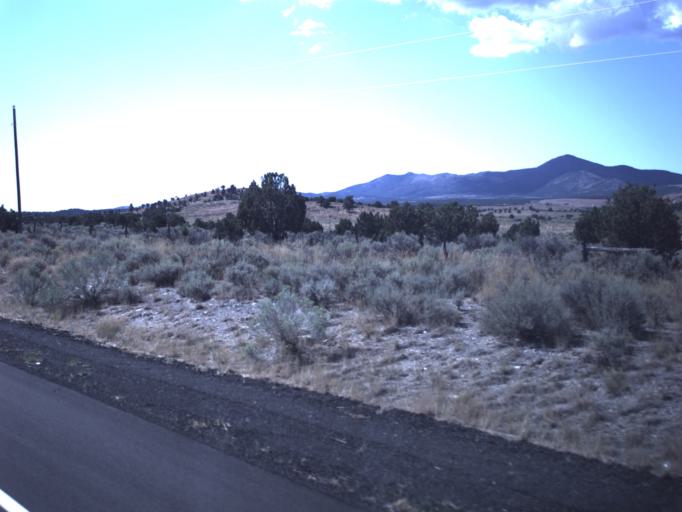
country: US
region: Utah
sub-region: Utah County
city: Eagle Mountain
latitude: 40.0440
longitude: -112.2921
